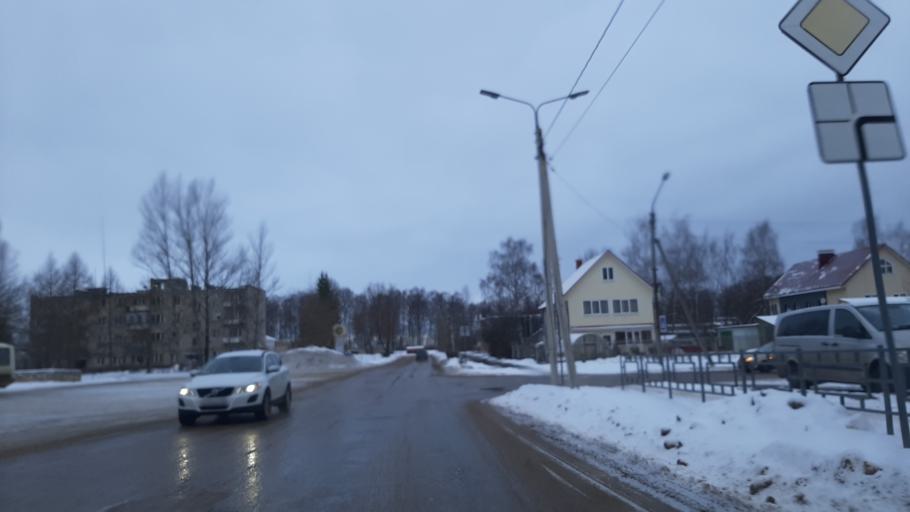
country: RU
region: Kostroma
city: Volgorechensk
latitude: 57.4433
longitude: 41.1477
